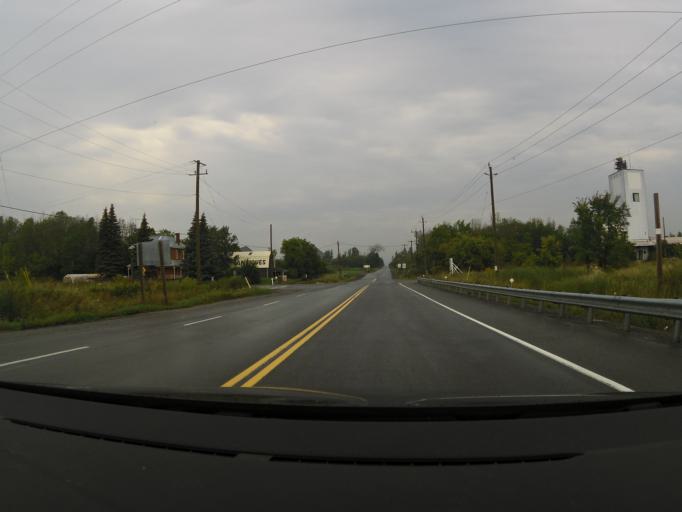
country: CA
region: Ontario
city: Carleton Place
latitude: 45.1731
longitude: -76.0526
